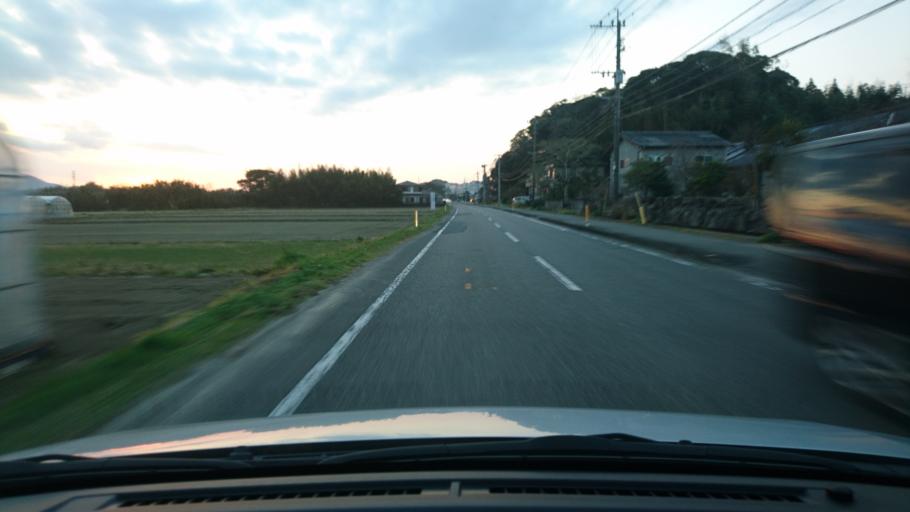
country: JP
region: Miyazaki
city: Miyazaki-shi
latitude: 31.8535
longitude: 131.4142
